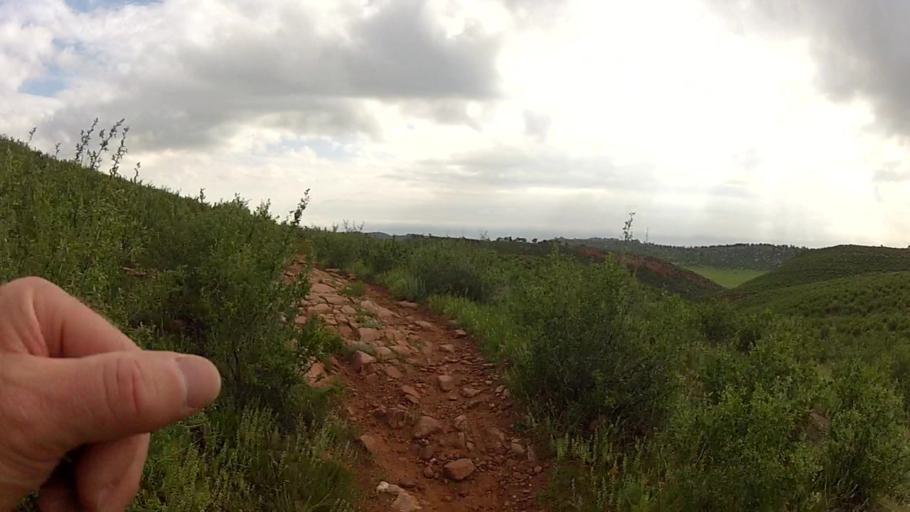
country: US
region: Colorado
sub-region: Larimer County
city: Loveland
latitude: 40.4378
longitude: -105.1570
